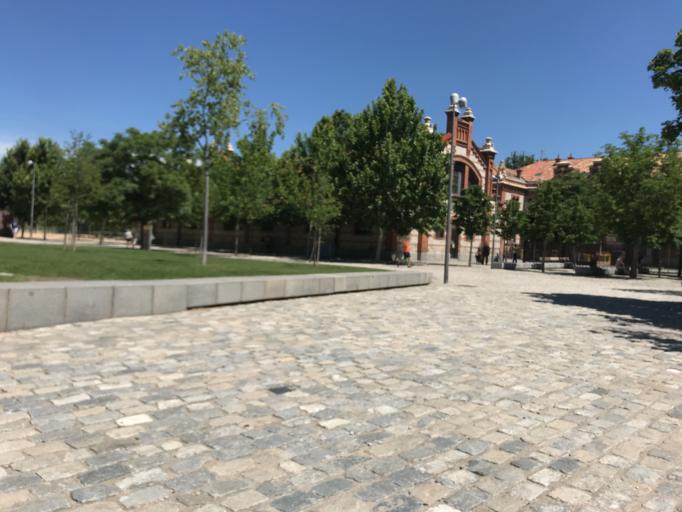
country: ES
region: Madrid
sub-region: Provincia de Madrid
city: Usera
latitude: 40.3920
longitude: -3.6999
